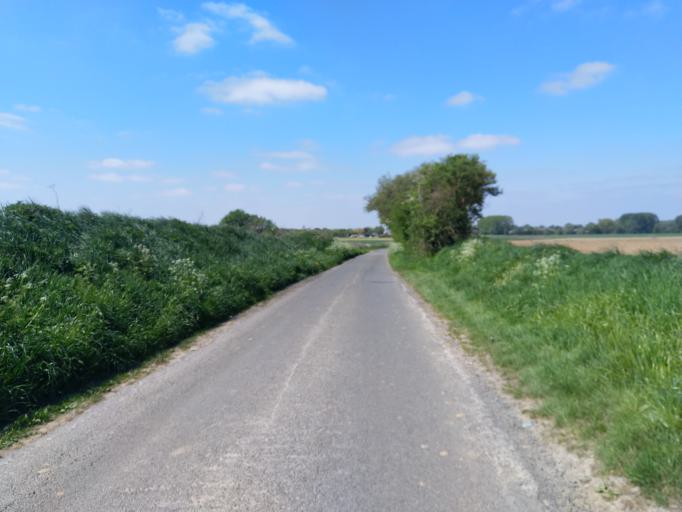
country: BE
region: Wallonia
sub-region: Province du Hainaut
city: Chievres
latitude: 50.5277
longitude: 3.8104
